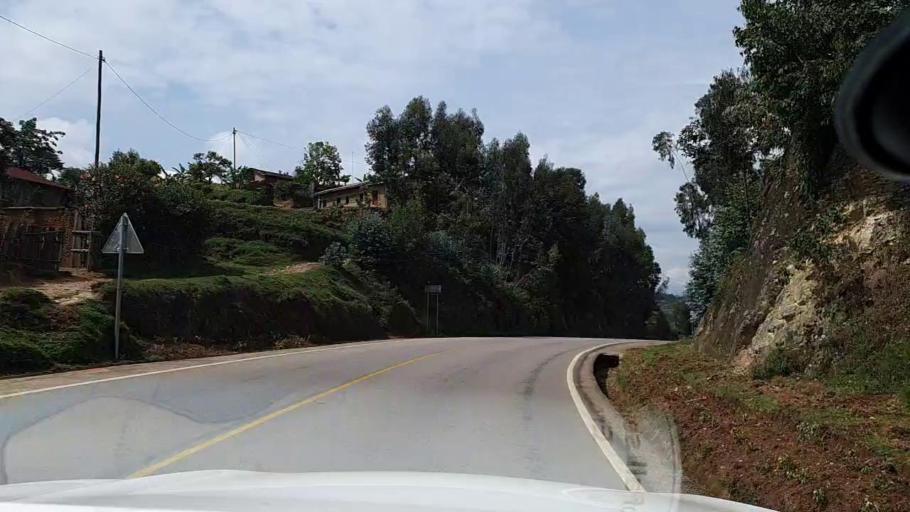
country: RW
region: Southern Province
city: Nzega
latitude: -2.4843
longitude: 29.5192
